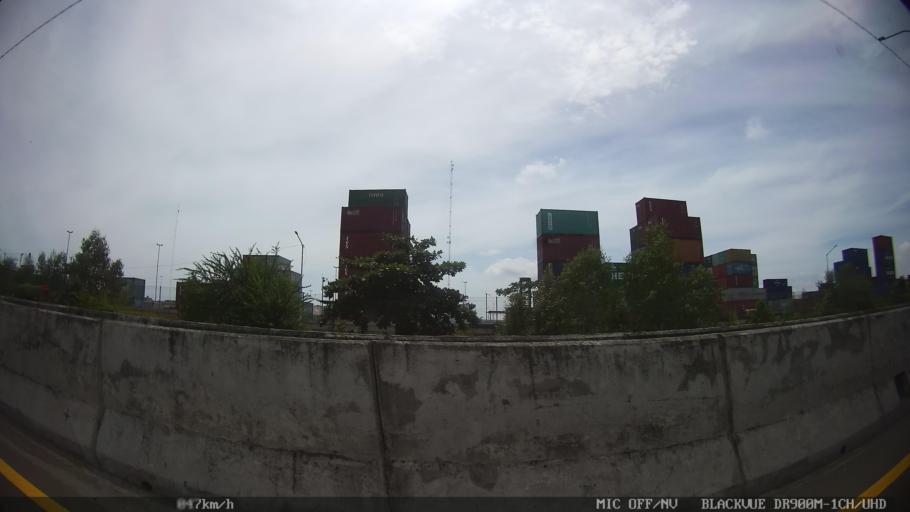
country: ID
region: North Sumatra
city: Belawan
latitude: 3.7682
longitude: 98.6844
